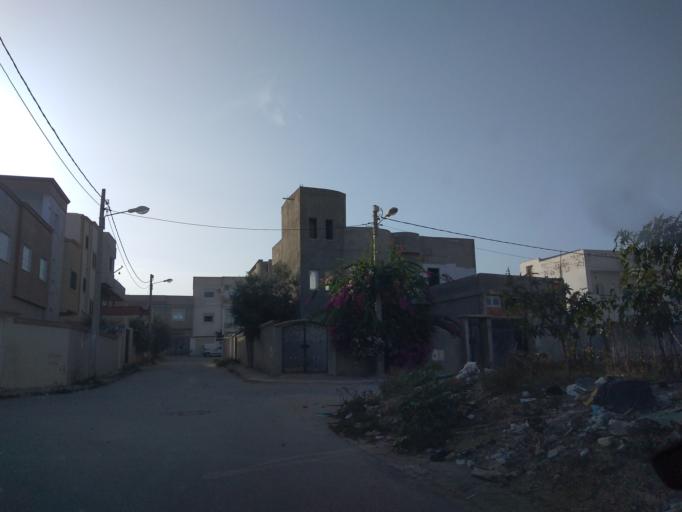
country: TN
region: Manouba
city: Manouba
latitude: 36.7942
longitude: 10.0868
